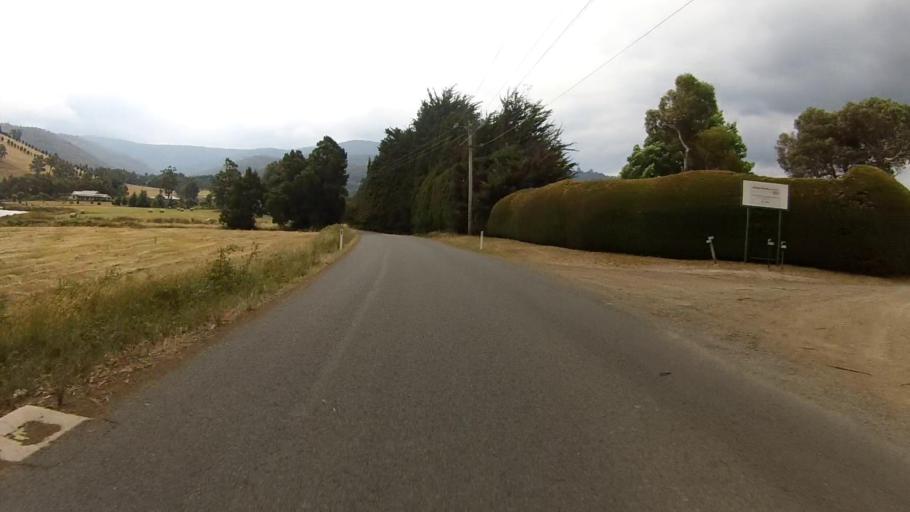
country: AU
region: Tasmania
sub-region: Huon Valley
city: Huonville
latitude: -42.9874
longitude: 147.0608
